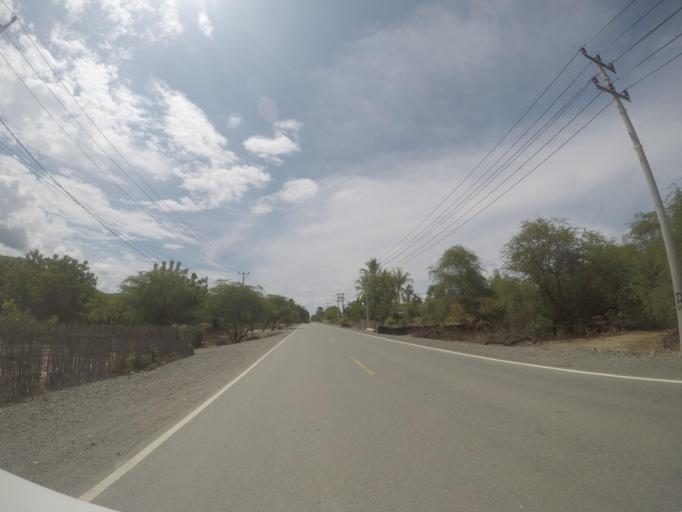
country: TL
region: Liquica
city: Liquica
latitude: -8.5662
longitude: 125.4237
